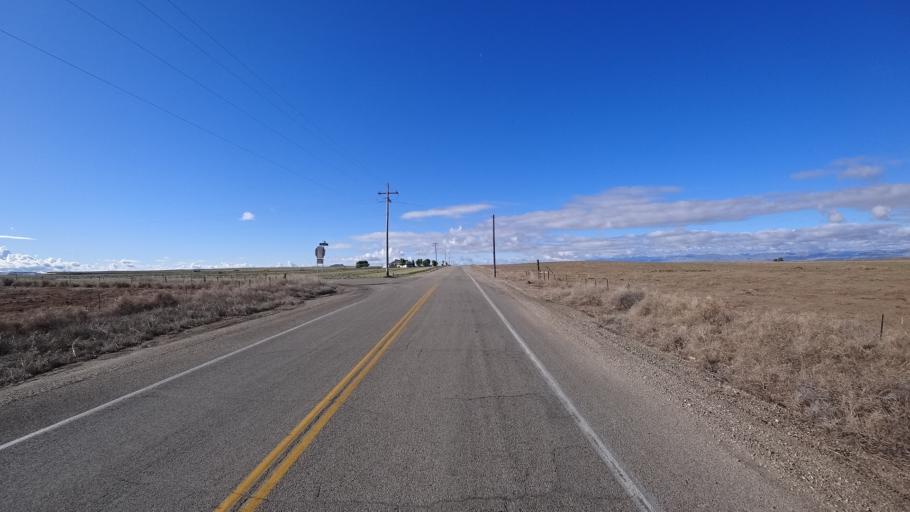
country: US
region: Idaho
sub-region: Ada County
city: Kuna
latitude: 43.4160
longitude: -116.4139
